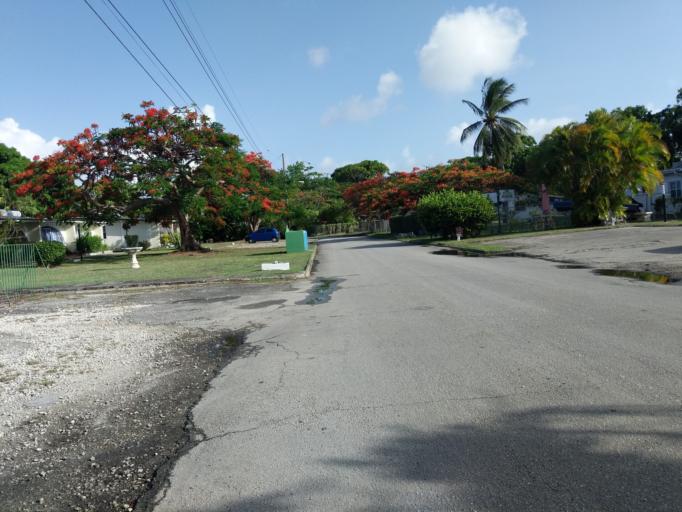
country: BB
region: Saint James
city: Holetown
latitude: 13.1809
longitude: -59.6381
